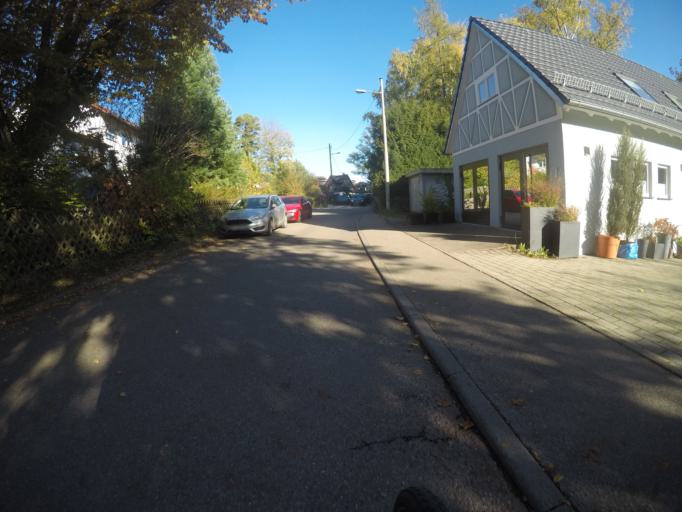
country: DE
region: Baden-Wuerttemberg
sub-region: Regierungsbezirk Stuttgart
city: Steinenbronn
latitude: 48.7159
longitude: 9.0999
